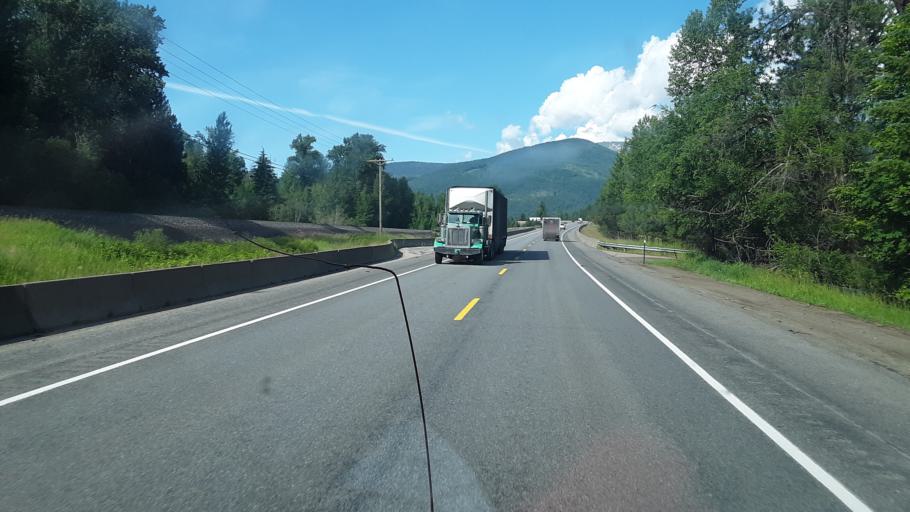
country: US
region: Idaho
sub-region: Bonner County
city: Ponderay
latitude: 48.4168
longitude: -116.5087
